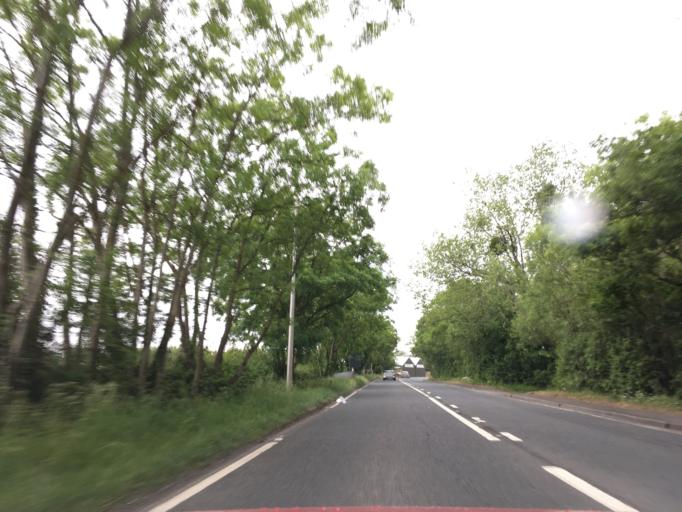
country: GB
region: England
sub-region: North Somerset
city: Kingston Seymour
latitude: 51.3756
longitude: -2.8529
